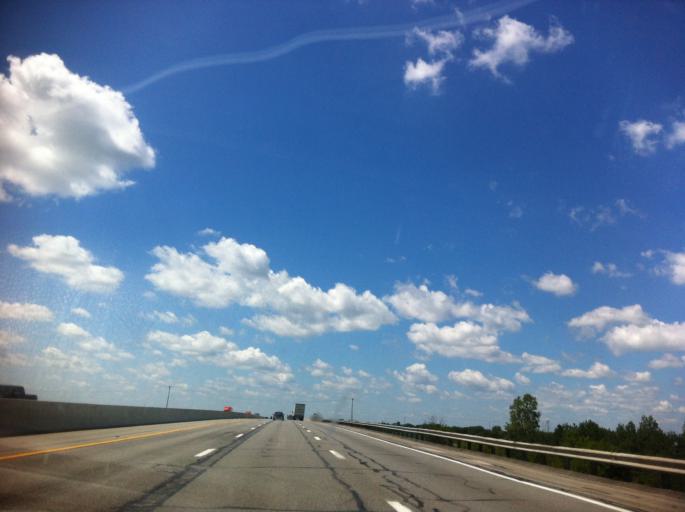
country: US
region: Ohio
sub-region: Wood County
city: Walbridge
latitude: 41.5394
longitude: -83.5064
